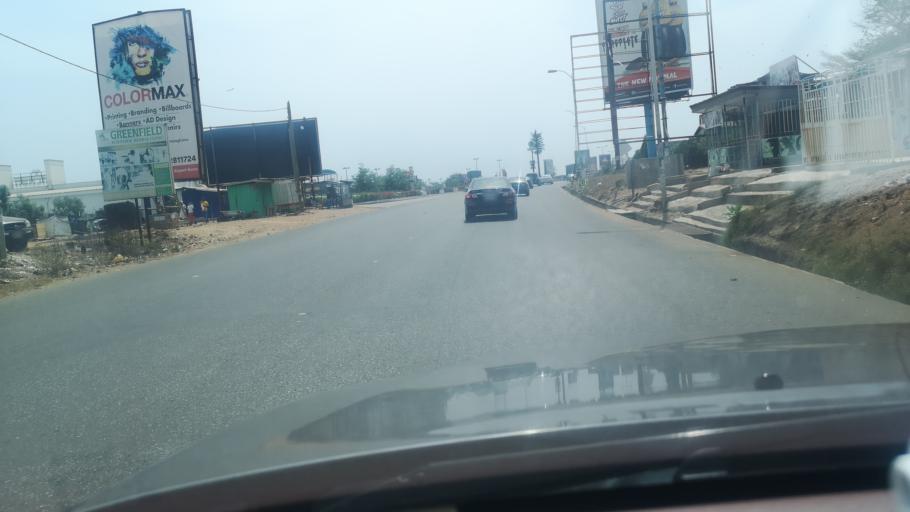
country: GH
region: Greater Accra
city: Nungua
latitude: 5.6145
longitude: -0.0705
